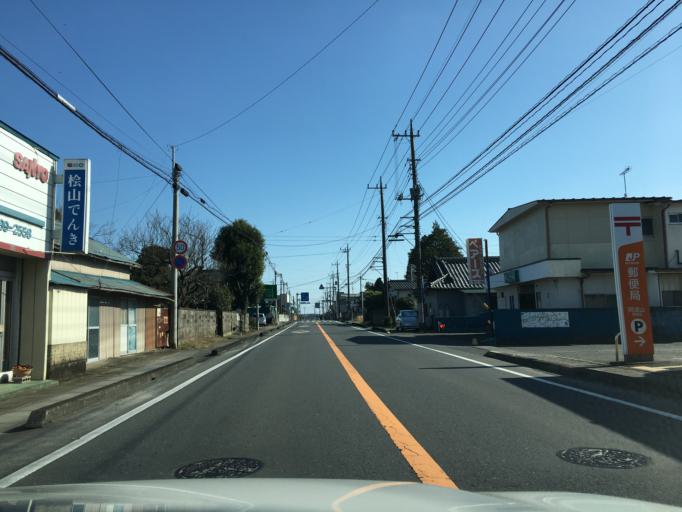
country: JP
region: Ibaraki
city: Omiya
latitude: 36.5159
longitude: 140.3658
